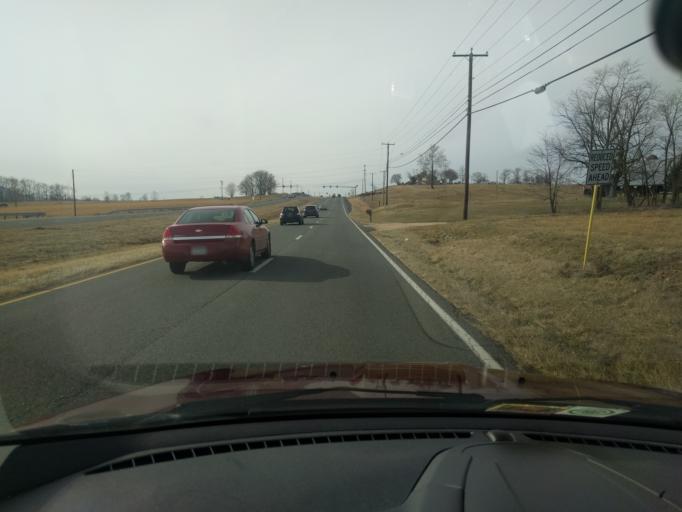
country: US
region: Virginia
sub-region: Augusta County
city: Stuarts Draft
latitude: 38.0450
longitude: -78.9936
